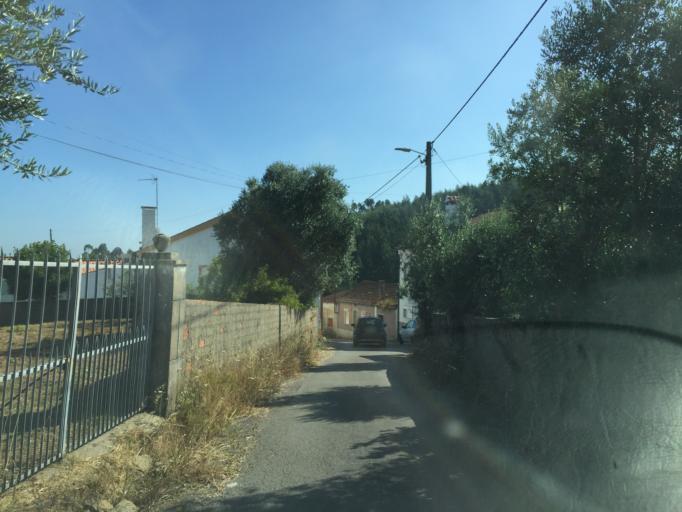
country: PT
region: Santarem
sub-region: Ferreira do Zezere
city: Ferreira do Zezere
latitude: 39.5998
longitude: -8.2976
